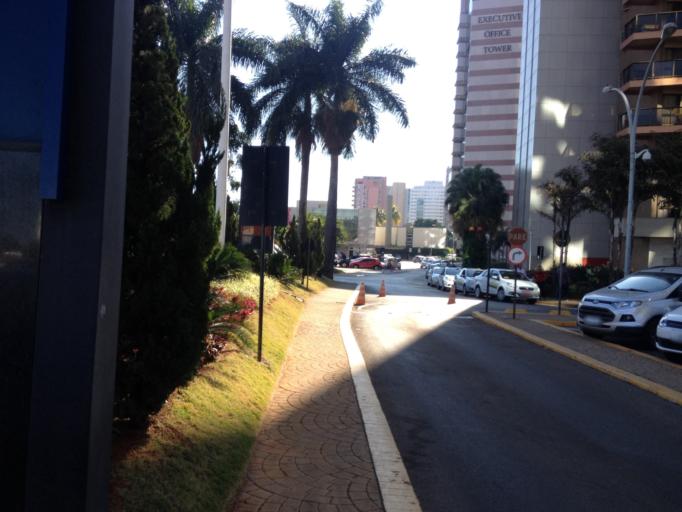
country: BR
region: Federal District
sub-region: Brasilia
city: Brasilia
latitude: -15.7908
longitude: -47.8865
